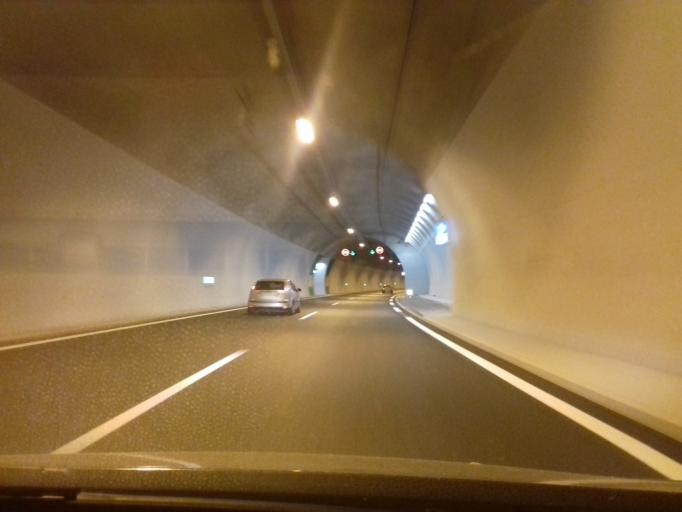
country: GR
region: West Greece
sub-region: Nomos Achaias
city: Akrata
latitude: 38.1674
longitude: 22.2736
